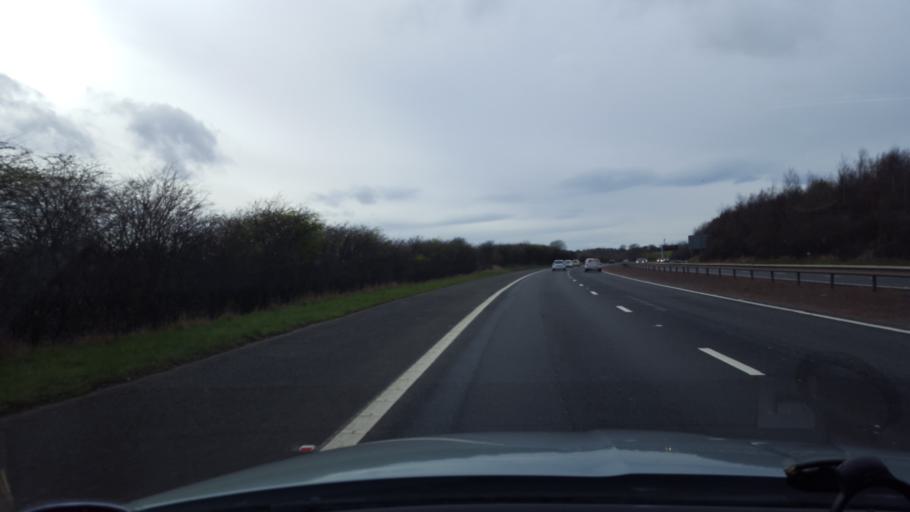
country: GB
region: Scotland
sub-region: Edinburgh
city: Currie
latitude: 55.9188
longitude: -3.3309
